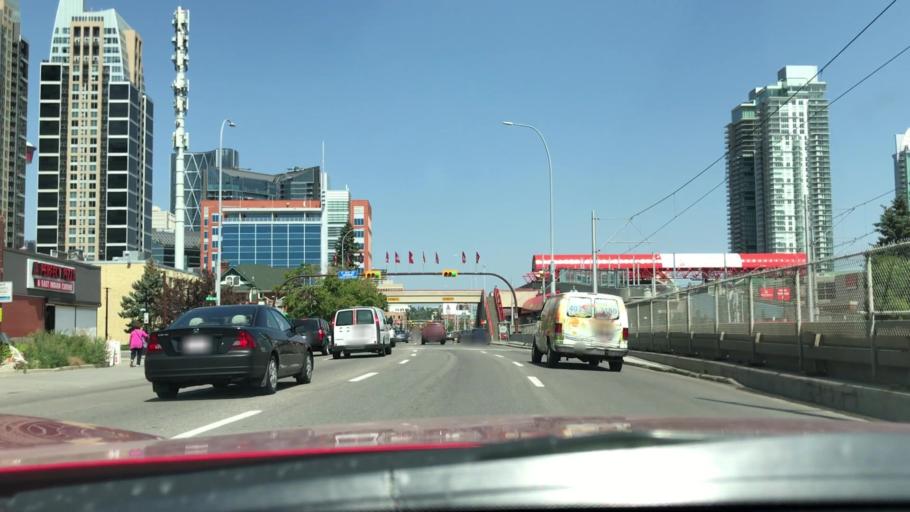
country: CA
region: Alberta
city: Calgary
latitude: 51.0373
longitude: -114.0587
